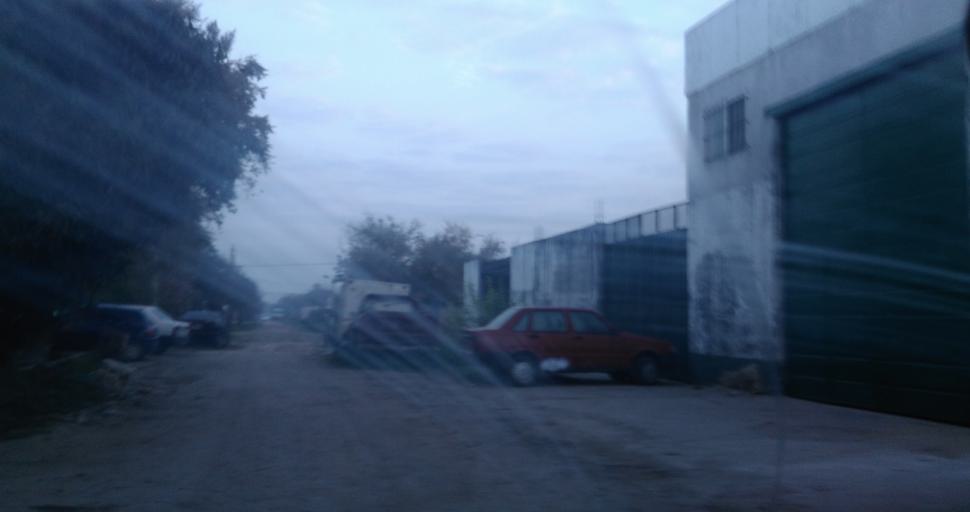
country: AR
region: Chaco
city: Fontana
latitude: -27.4527
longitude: -59.0320
